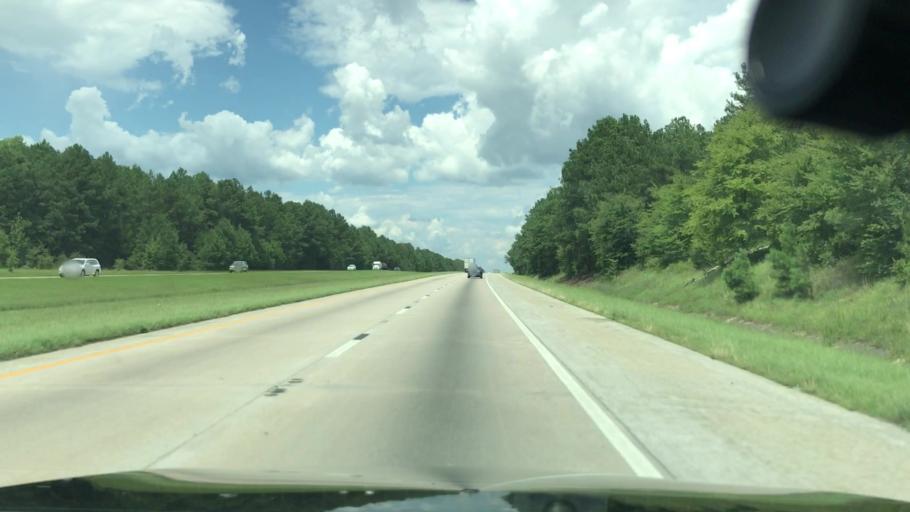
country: US
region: South Carolina
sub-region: Fairfield County
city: Winnsboro
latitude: 34.4242
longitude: -80.9958
